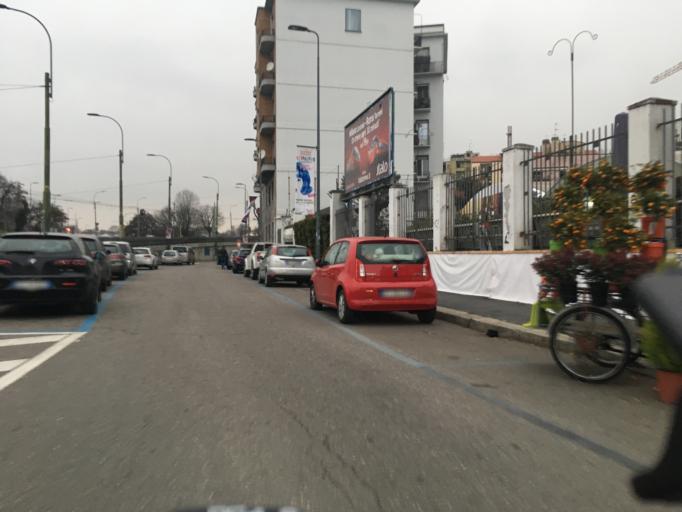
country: IT
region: Lombardy
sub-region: Citta metropolitana di Milano
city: Milano
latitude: 45.4465
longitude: 9.1595
